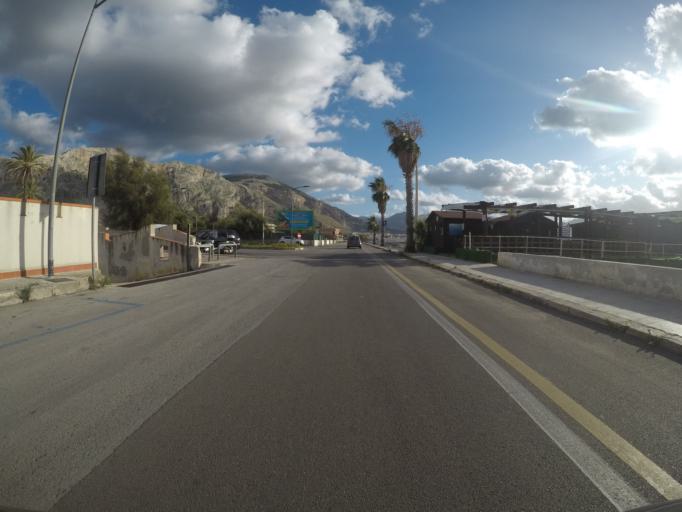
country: IT
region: Sicily
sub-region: Palermo
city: Isola delle Femmine
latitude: 38.1986
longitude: 13.2437
